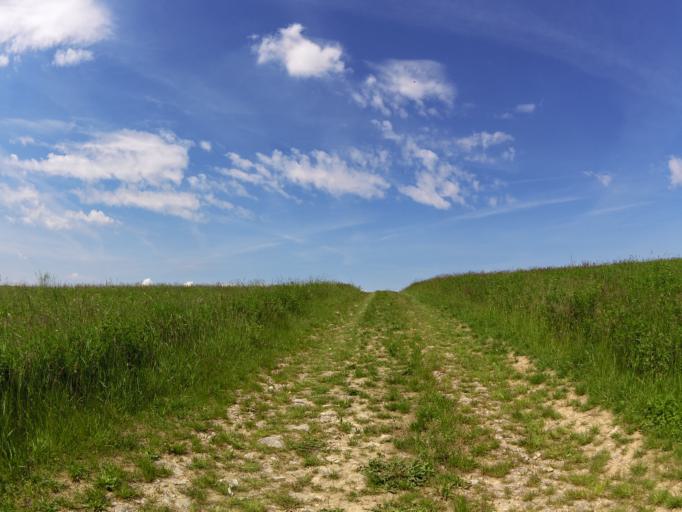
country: DE
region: Bavaria
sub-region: Regierungsbezirk Unterfranken
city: Theilheim
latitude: 49.7349
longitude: 10.0391
